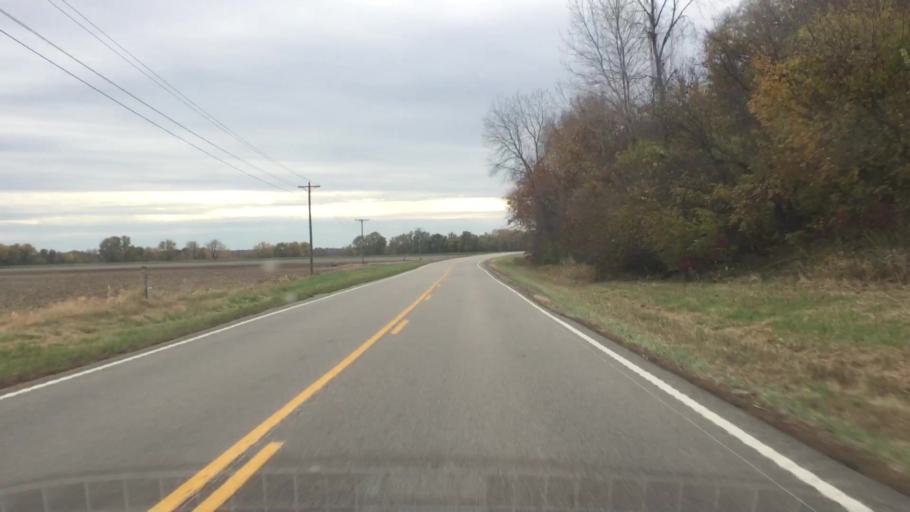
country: US
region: Missouri
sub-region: Callaway County
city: Holts Summit
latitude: 38.5836
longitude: -92.0544
